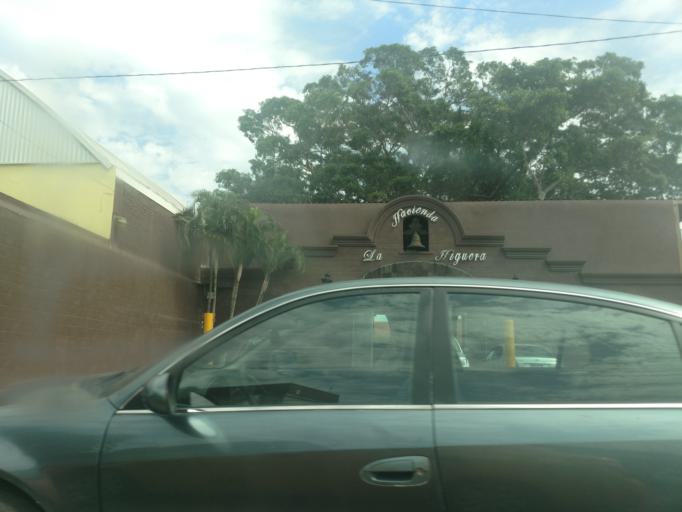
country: MX
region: Nayarit
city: Tepic
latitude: 21.4982
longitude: -104.8811
